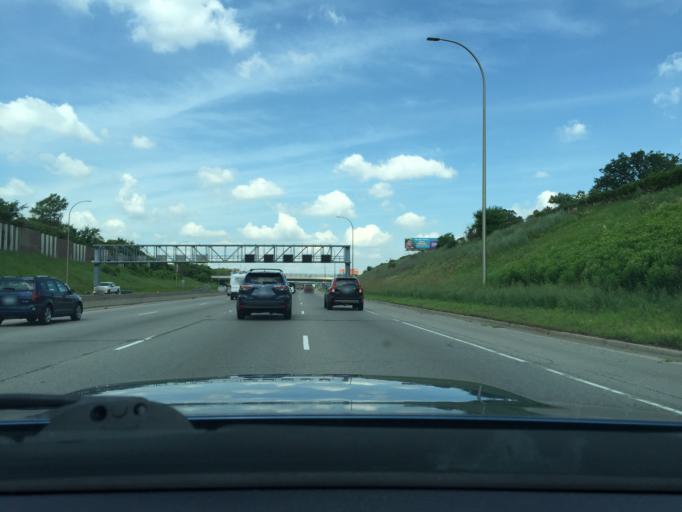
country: US
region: Minnesota
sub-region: Ramsey County
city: Falcon Heights
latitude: 44.9533
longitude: -93.1834
